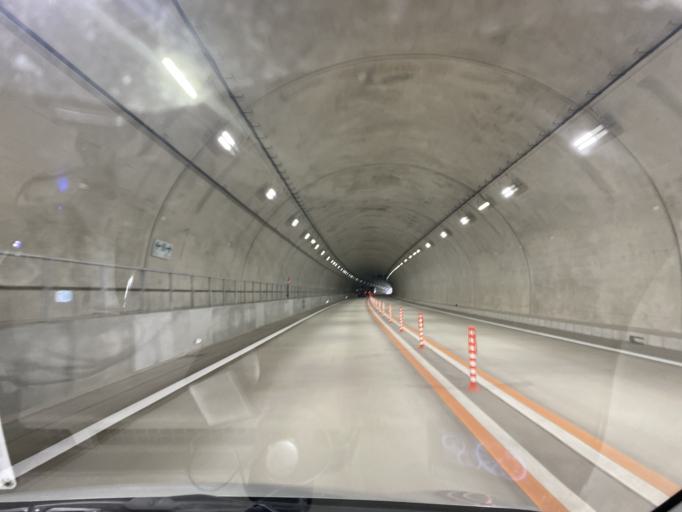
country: JP
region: Hyogo
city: Toyooka
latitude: 35.4953
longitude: 134.7851
